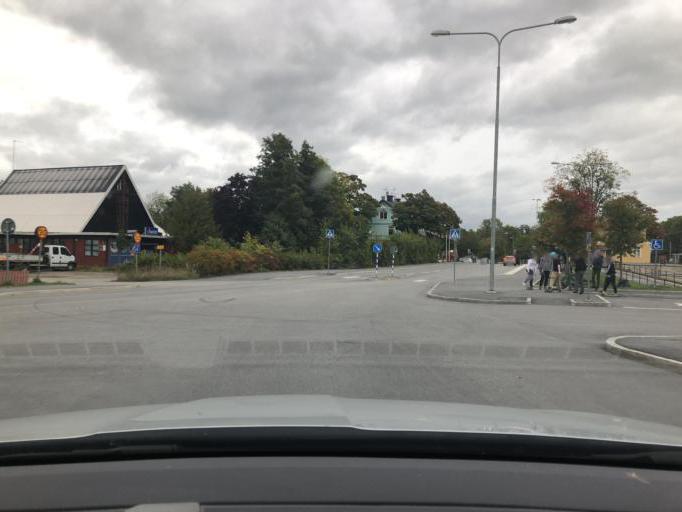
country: SE
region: Stockholm
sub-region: Haninge Kommun
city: Jordbro
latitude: 59.1020
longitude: 18.0421
